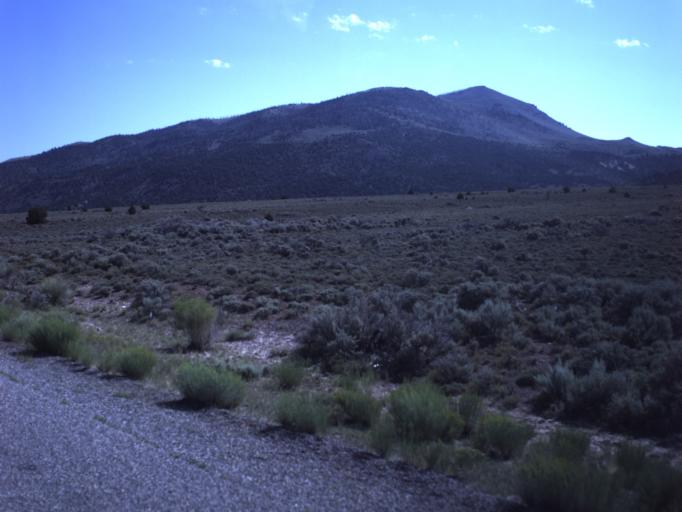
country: US
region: Utah
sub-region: Wayne County
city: Loa
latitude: 38.4994
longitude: -111.5343
